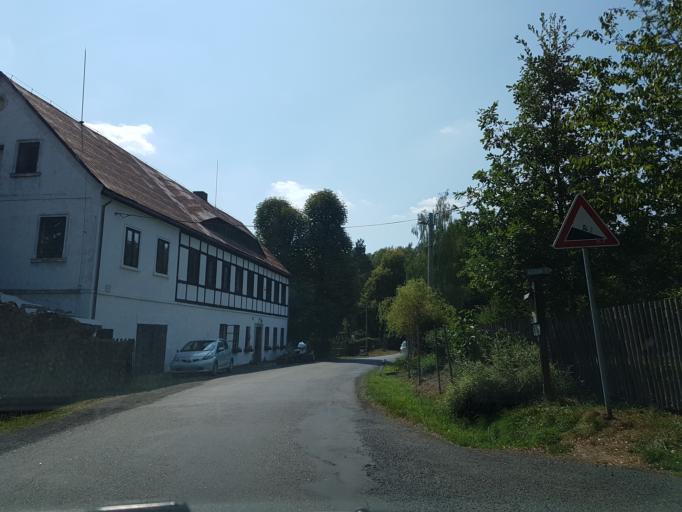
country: CZ
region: Ustecky
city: Ceska Kamenice
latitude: 50.8494
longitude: 14.4196
